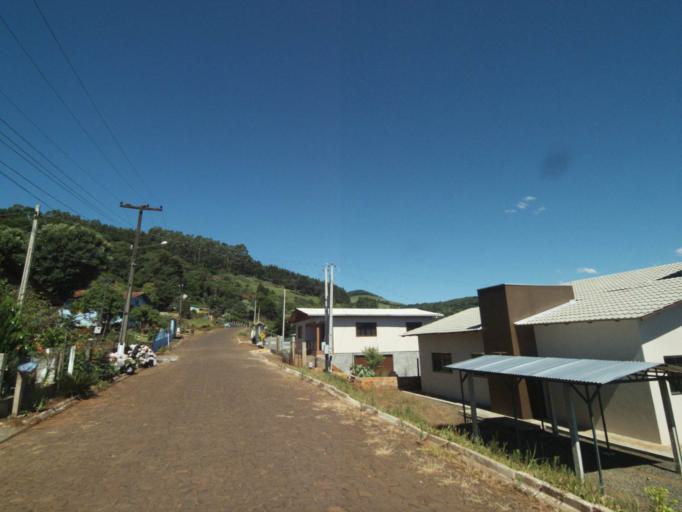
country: BR
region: Parana
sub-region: Ampere
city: Ampere
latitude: -26.1732
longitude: -53.3571
